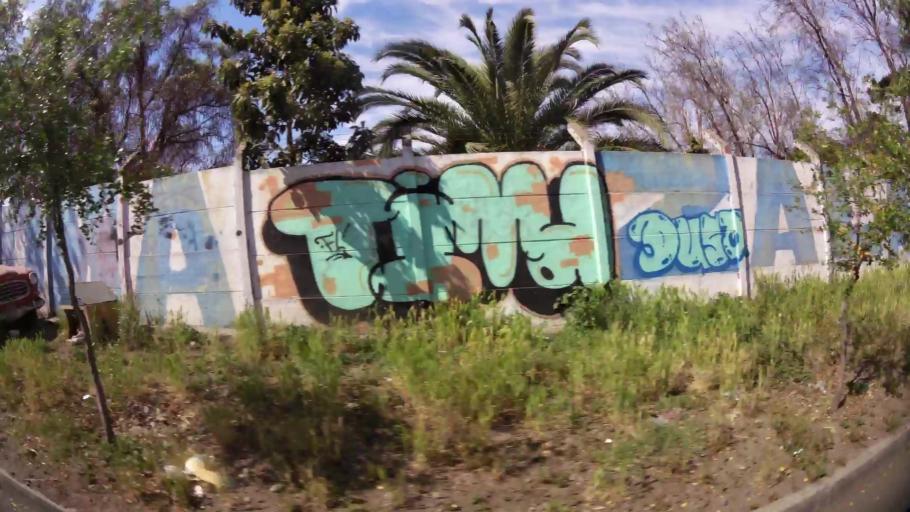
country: CL
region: Santiago Metropolitan
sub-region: Provincia de Talagante
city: Talagante
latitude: -33.6711
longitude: -70.9282
